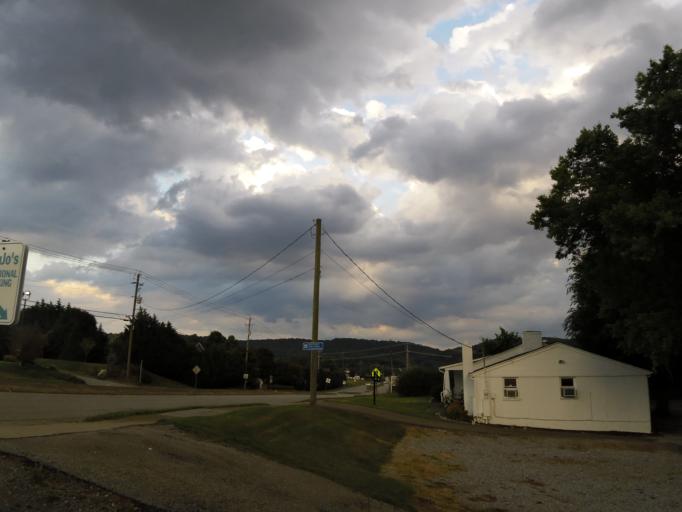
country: US
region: Tennessee
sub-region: Knox County
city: Knoxville
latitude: 36.0623
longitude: -83.9773
